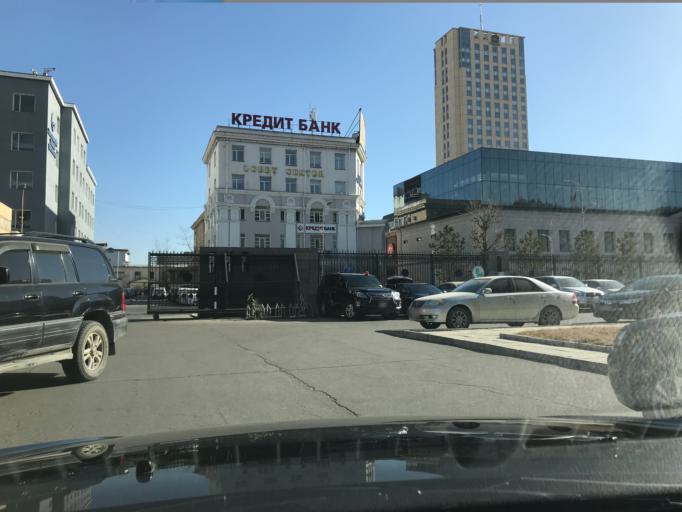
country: MN
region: Ulaanbaatar
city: Ulaanbaatar
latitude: 47.9214
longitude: 106.9180
